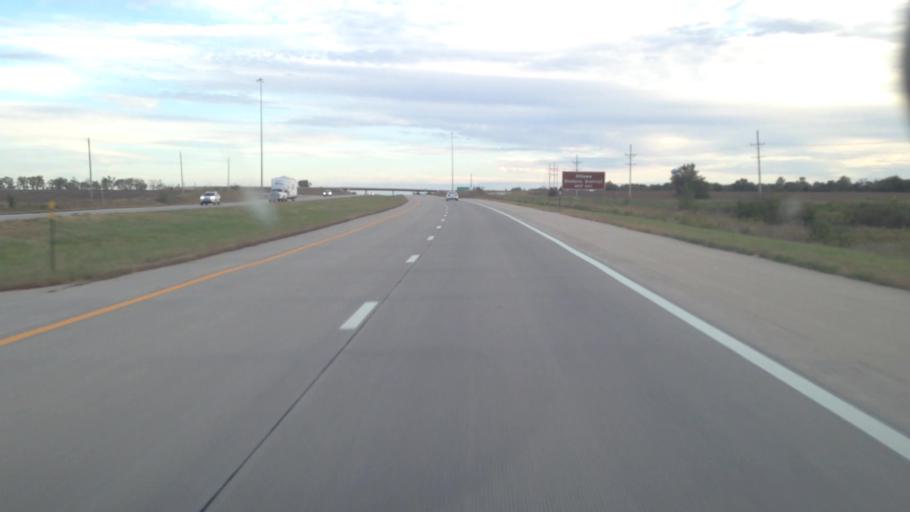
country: US
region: Kansas
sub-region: Franklin County
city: Ottawa
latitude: 38.6957
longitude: -95.2680
